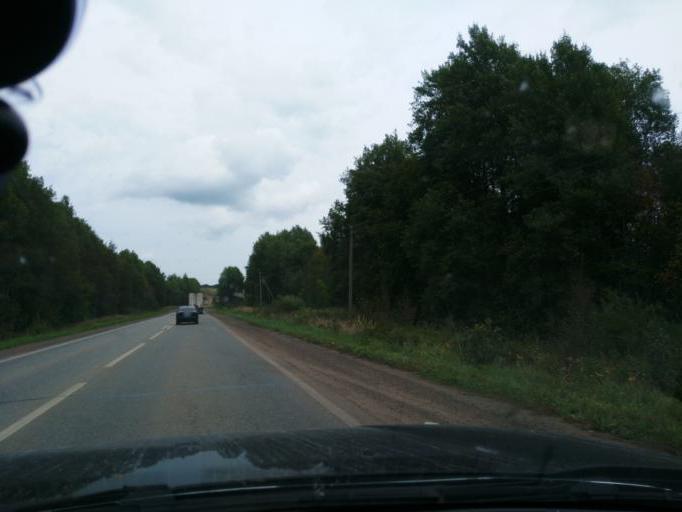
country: RU
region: Perm
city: Kuyeda
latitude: 56.4575
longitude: 55.6248
